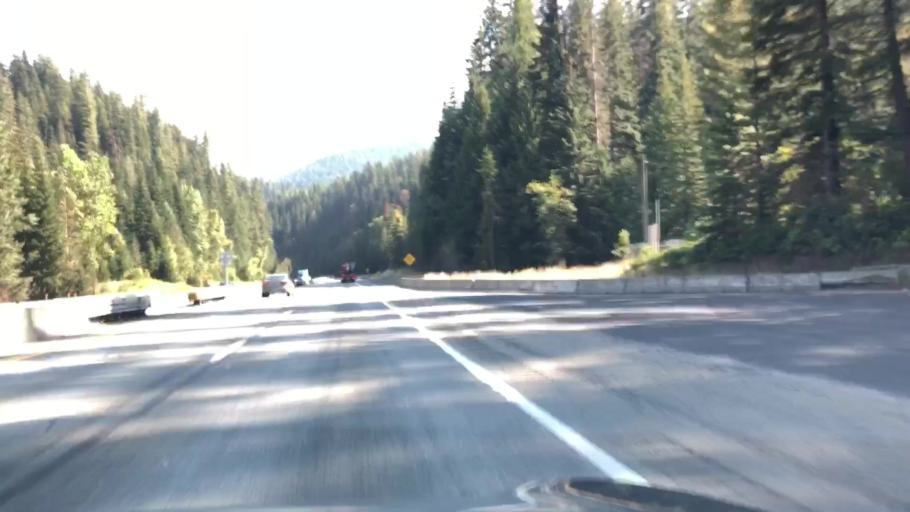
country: US
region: Idaho
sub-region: Shoshone County
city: Pinehurst
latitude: 47.6028
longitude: -116.4991
